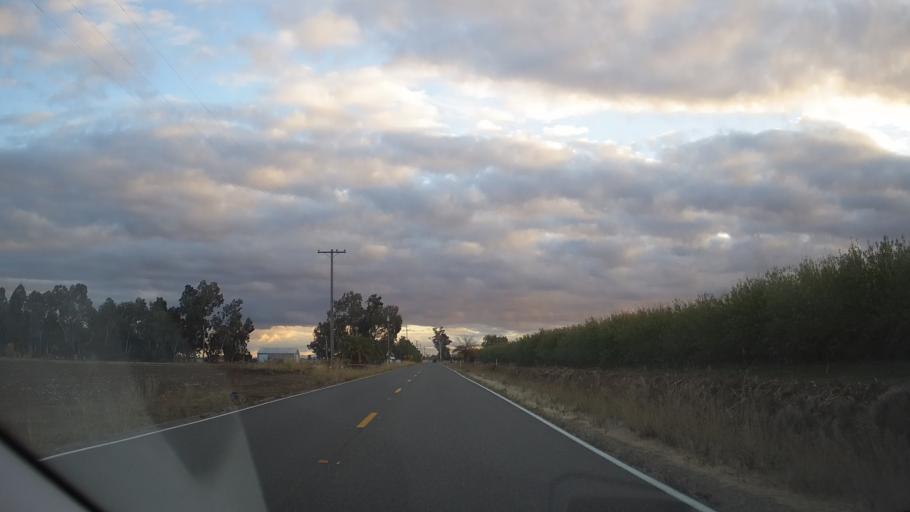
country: US
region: California
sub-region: Solano County
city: Hartley
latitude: 38.3868
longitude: -121.9059
